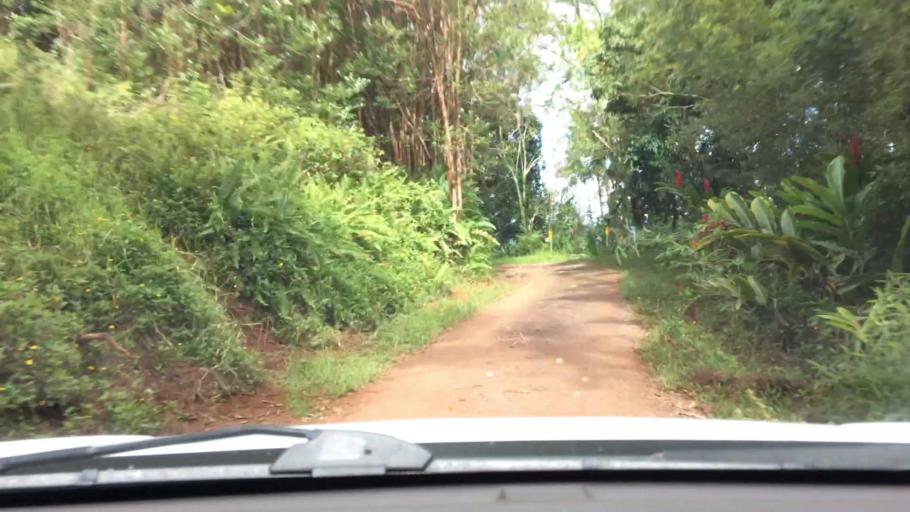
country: US
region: Hawaii
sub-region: Hawaii County
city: Pepeekeo
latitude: 19.8263
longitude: -155.1120
